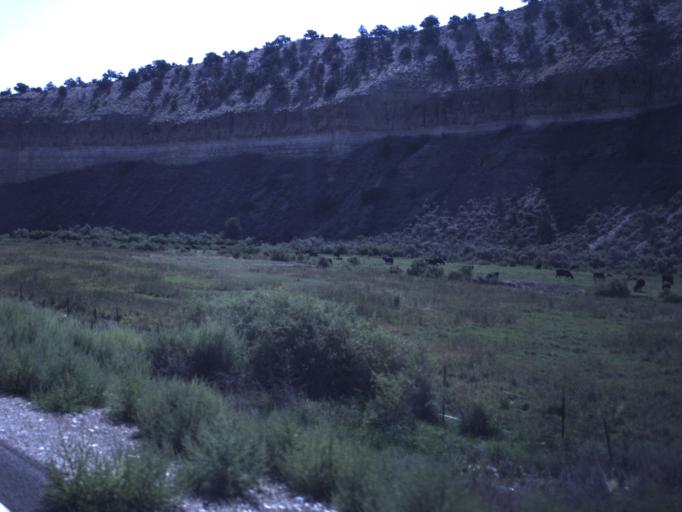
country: US
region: Utah
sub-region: Duchesne County
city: Duchesne
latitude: 40.1042
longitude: -110.4715
